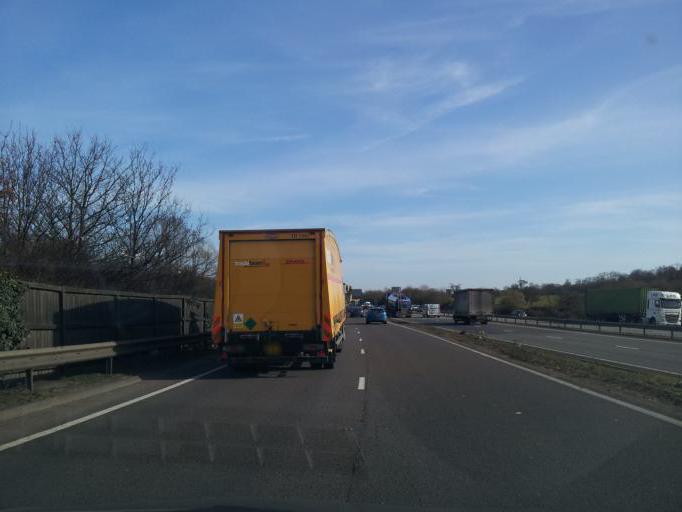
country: GB
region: England
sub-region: Cambridgeshire
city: Great Stukeley
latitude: 52.3395
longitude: -0.2059
